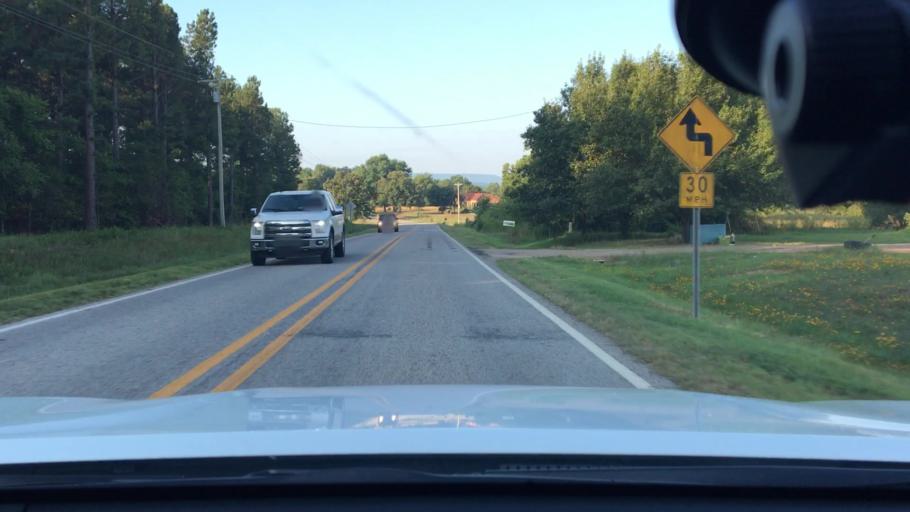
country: US
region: Arkansas
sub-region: Johnson County
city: Coal Hill
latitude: 35.3447
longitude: -93.5956
